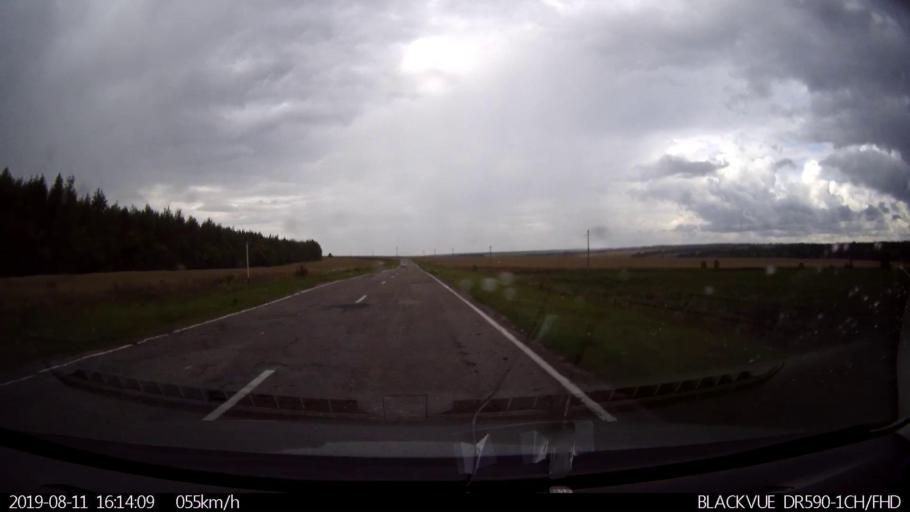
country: RU
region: Ulyanovsk
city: Ignatovka
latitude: 54.0256
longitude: 47.6348
